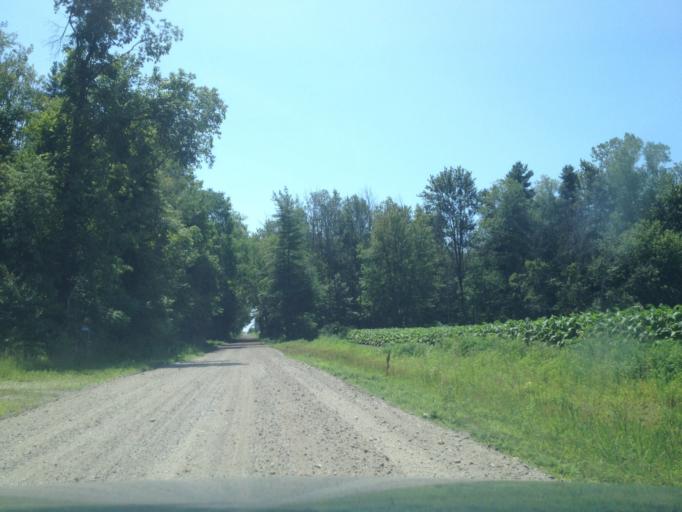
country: CA
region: Ontario
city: Aylmer
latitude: 42.6480
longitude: -80.7705
